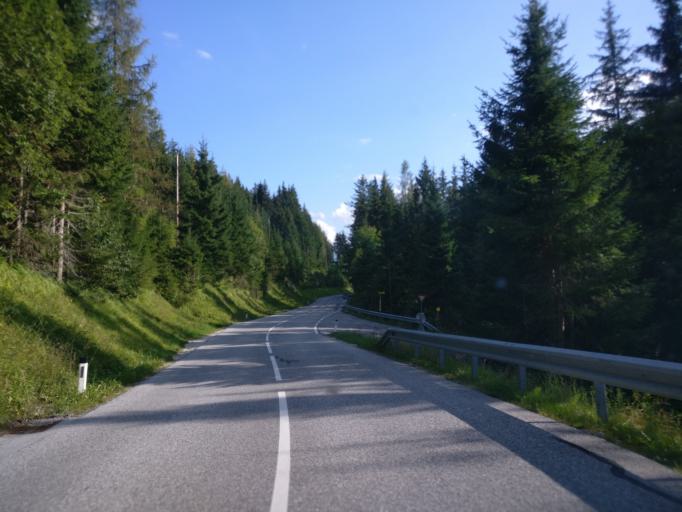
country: AT
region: Salzburg
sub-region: Politischer Bezirk Sankt Johann im Pongau
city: Muhlbach am Hochkonig
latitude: 47.3977
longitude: 13.1140
